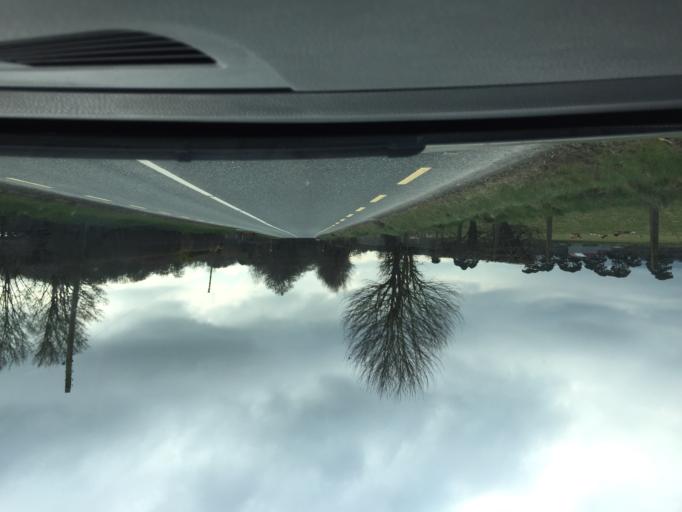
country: IE
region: Leinster
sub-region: South Dublin
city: Rathcoole
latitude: 53.2248
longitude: -6.4662
